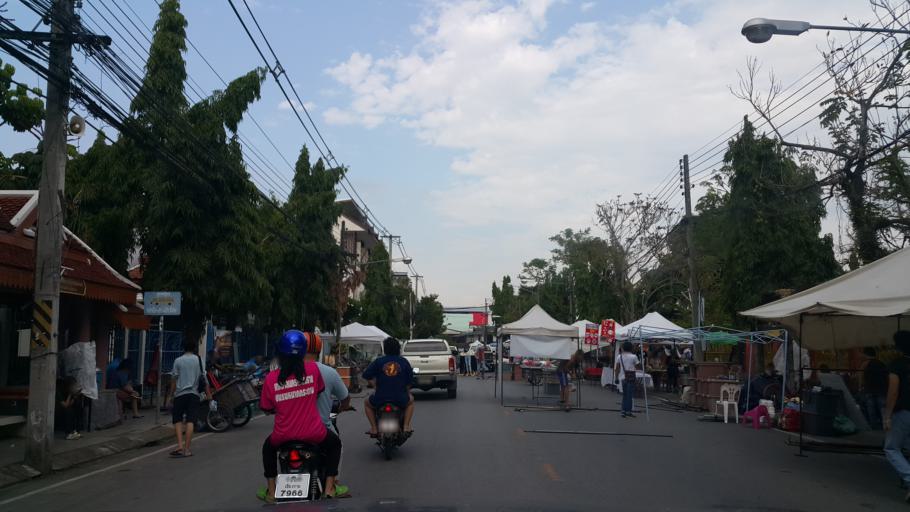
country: TH
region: Chiang Rai
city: Chiang Rai
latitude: 19.9089
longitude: 99.8365
